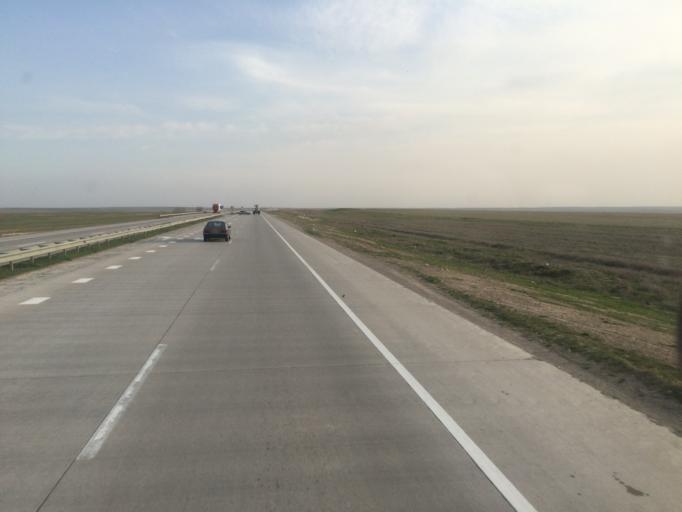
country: KZ
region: Ongtustik Qazaqstan
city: Temirlanovka
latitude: 42.7365
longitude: 69.2079
